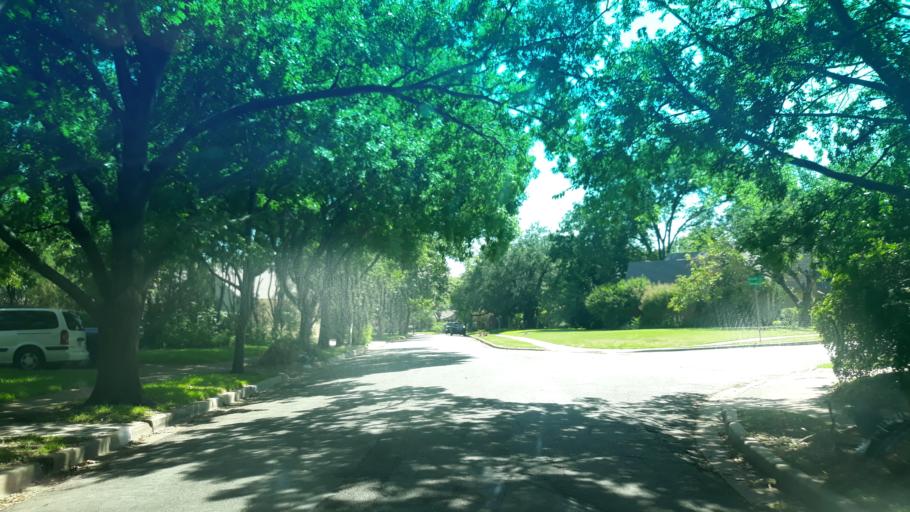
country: US
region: Texas
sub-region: Dallas County
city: Highland Park
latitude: 32.8202
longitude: -96.7507
